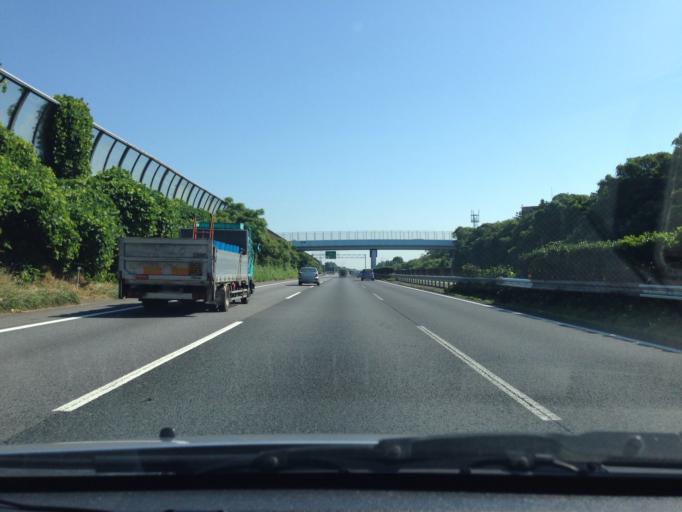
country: JP
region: Ibaraki
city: Naka
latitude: 36.1143
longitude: 140.1811
